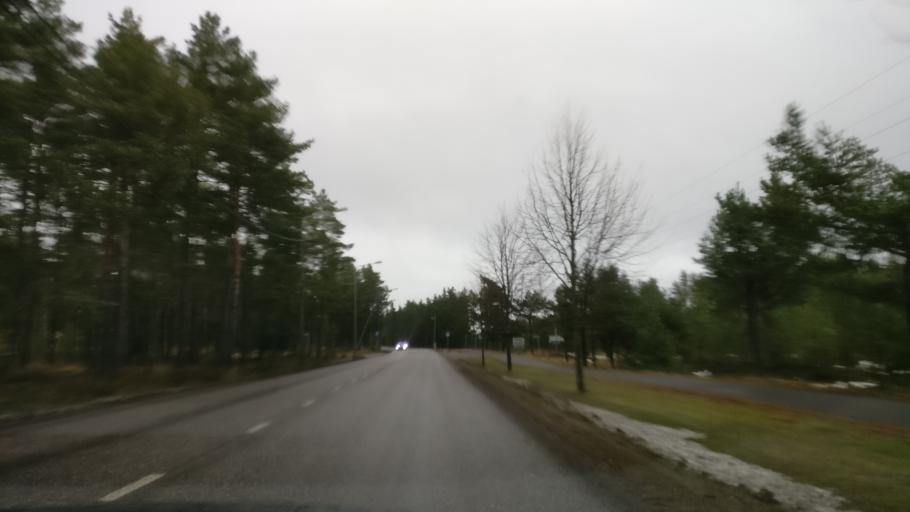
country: FI
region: Uusimaa
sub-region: Raaseporin
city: Hanko
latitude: 59.8416
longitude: 23.0038
